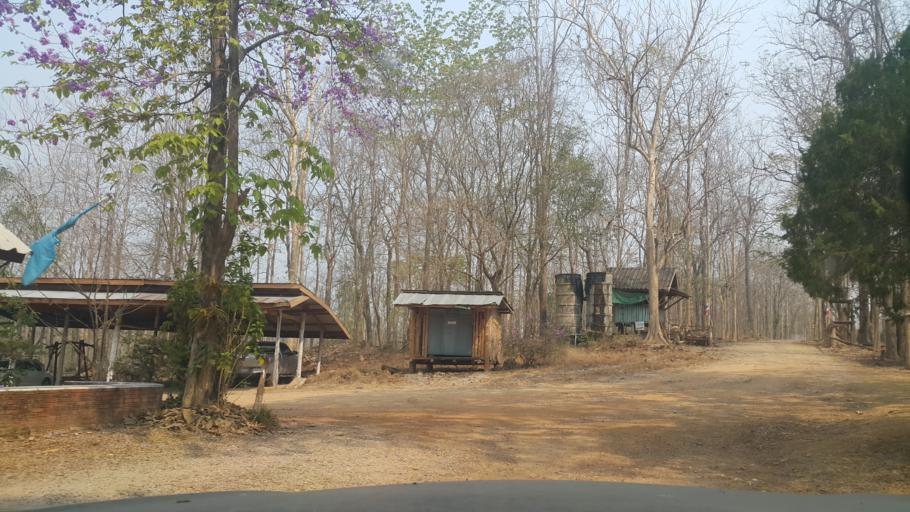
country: TH
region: Lampang
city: Thoen
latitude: 17.5273
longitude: 99.3456
